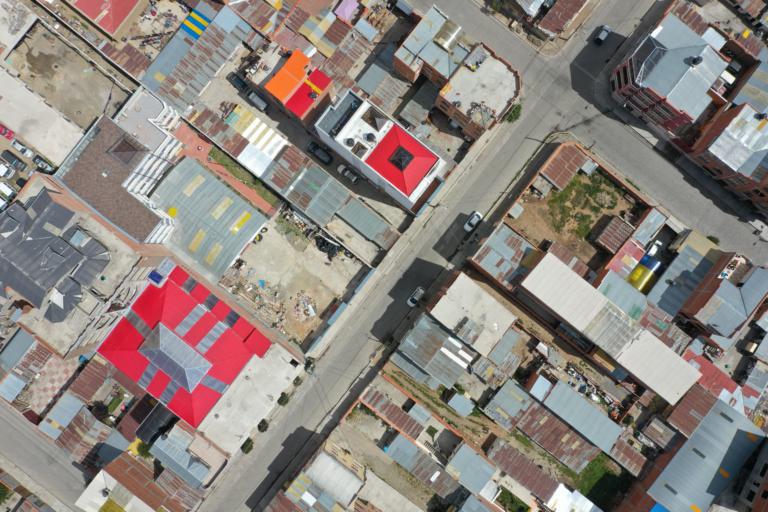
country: BO
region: La Paz
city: La Paz
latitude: -16.5219
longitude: -68.1589
